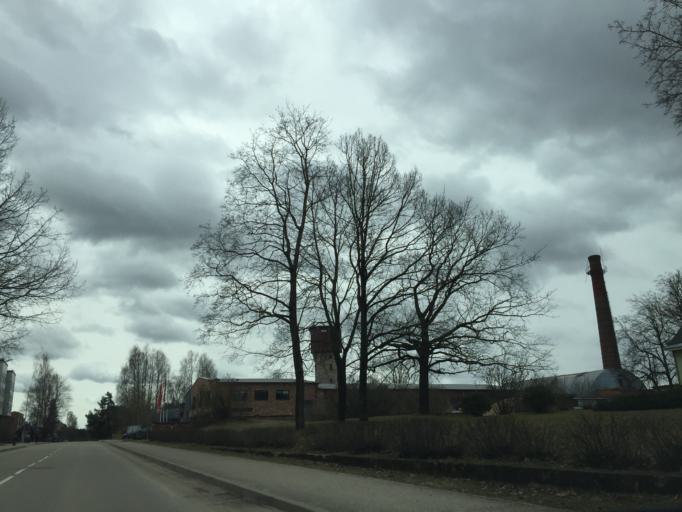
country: LV
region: Livani
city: Livani
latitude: 56.3533
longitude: 26.1734
